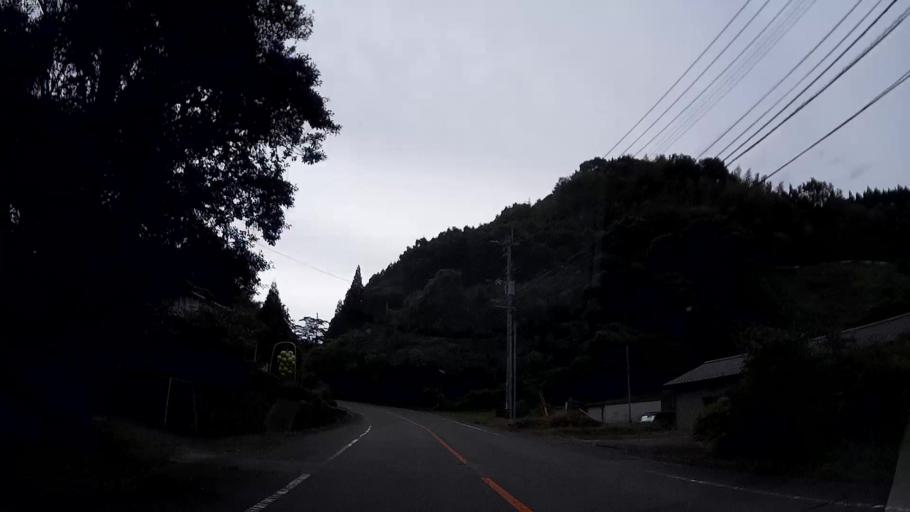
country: JP
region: Kumamoto
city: Kikuchi
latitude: 33.0145
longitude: 130.8823
